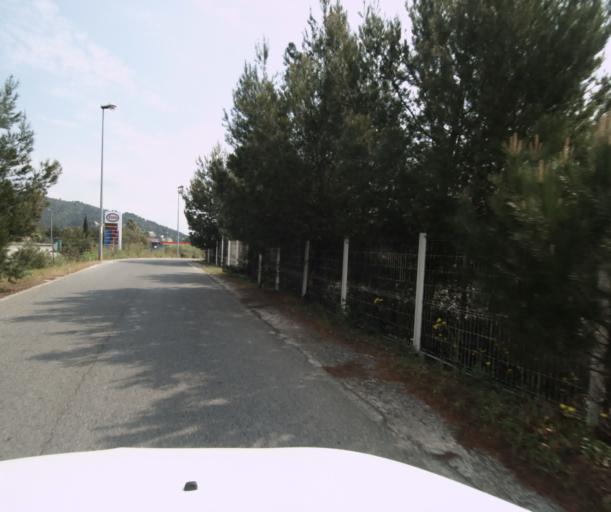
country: FR
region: Provence-Alpes-Cote d'Azur
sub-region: Departement du Var
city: La Garde
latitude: 43.1424
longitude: 6.0087
